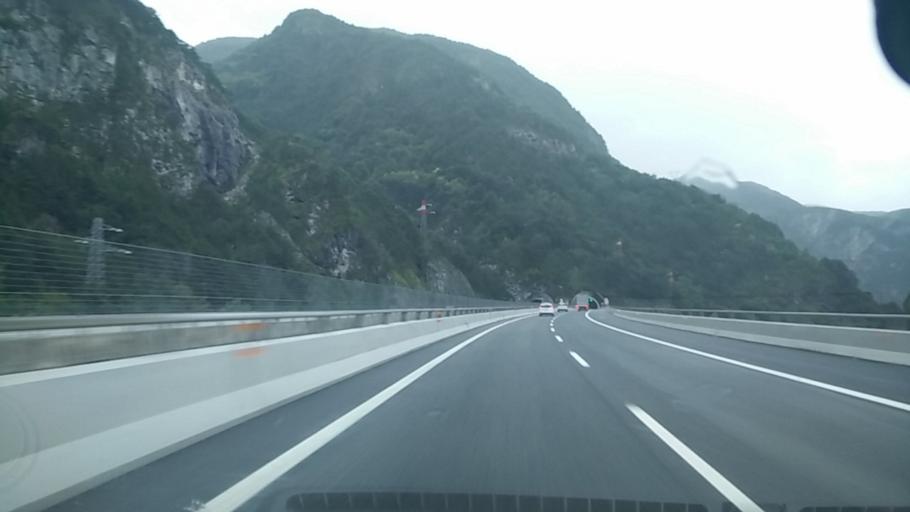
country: IT
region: Friuli Venezia Giulia
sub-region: Provincia di Udine
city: Chiusaforte
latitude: 46.4227
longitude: 13.3195
